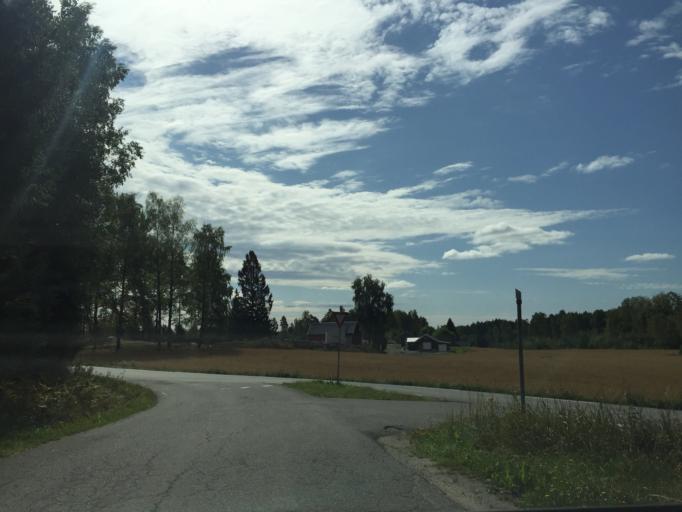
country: NO
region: Akershus
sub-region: Ski
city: Ski
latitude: 59.6513
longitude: 10.8727
